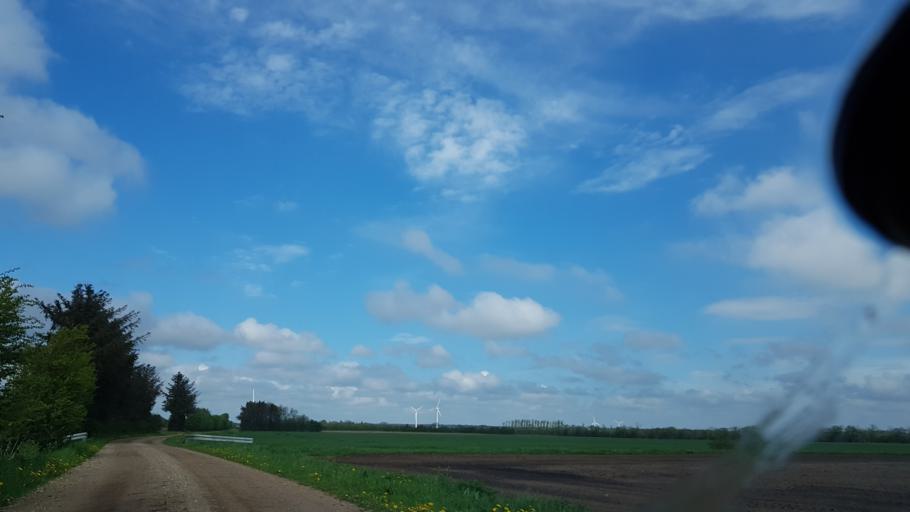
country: DK
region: South Denmark
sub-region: Tonder Kommune
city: Sherrebek
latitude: 55.0859
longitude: 8.8446
